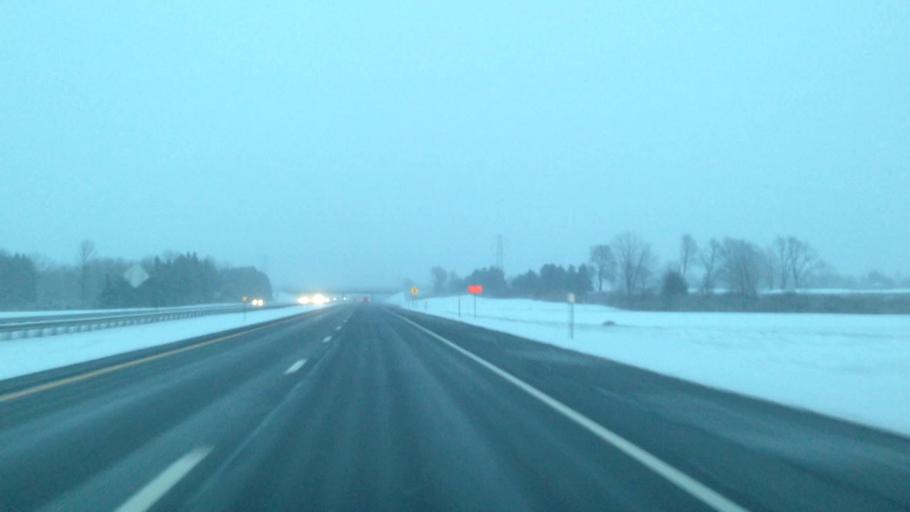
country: US
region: New York
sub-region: Oneida County
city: Sherrill
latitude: 43.1238
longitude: -75.5812
